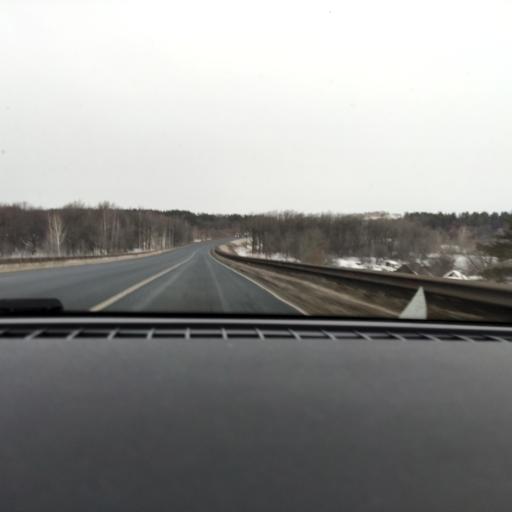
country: RU
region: Samara
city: Novosemeykino
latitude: 53.3566
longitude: 50.4441
